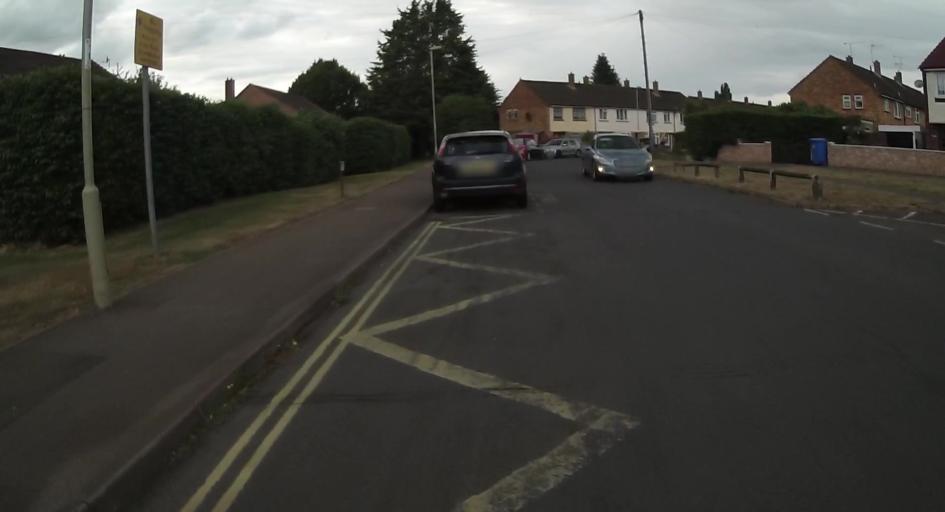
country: GB
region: England
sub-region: Surrey
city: Seale
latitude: 51.2377
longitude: -0.7403
